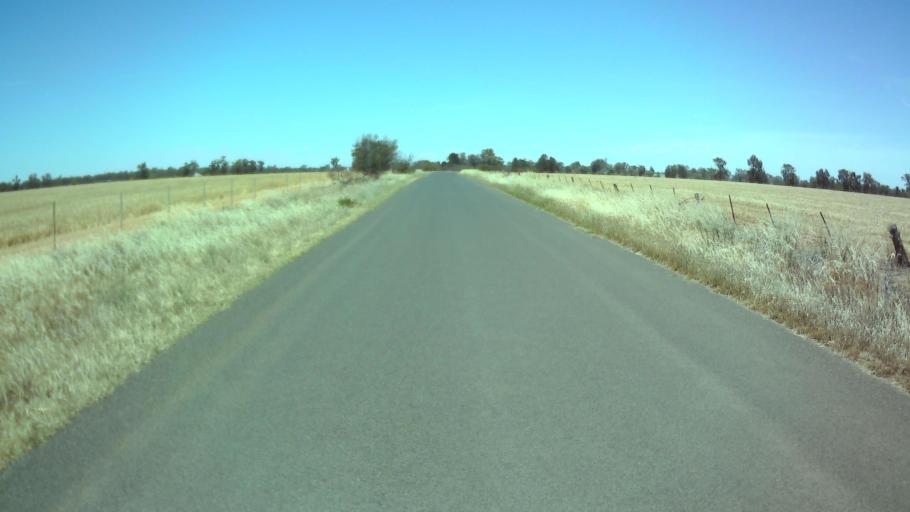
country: AU
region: New South Wales
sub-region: Weddin
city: Grenfell
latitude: -34.0534
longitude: 147.7812
